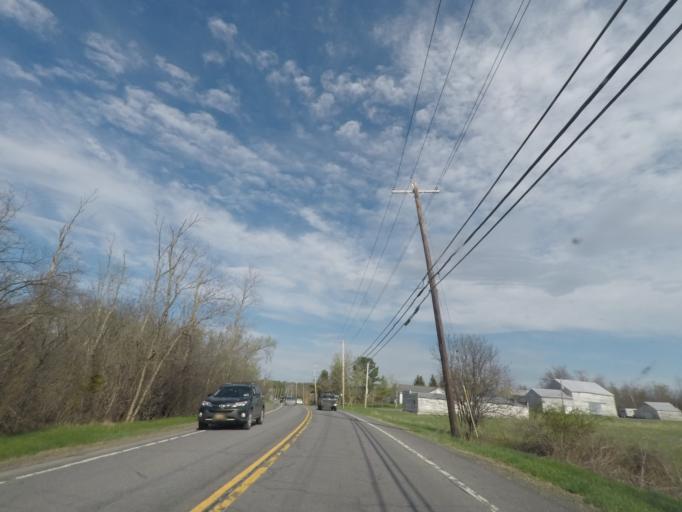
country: US
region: New York
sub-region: Albany County
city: Voorheesville
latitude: 42.6240
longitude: -73.9434
